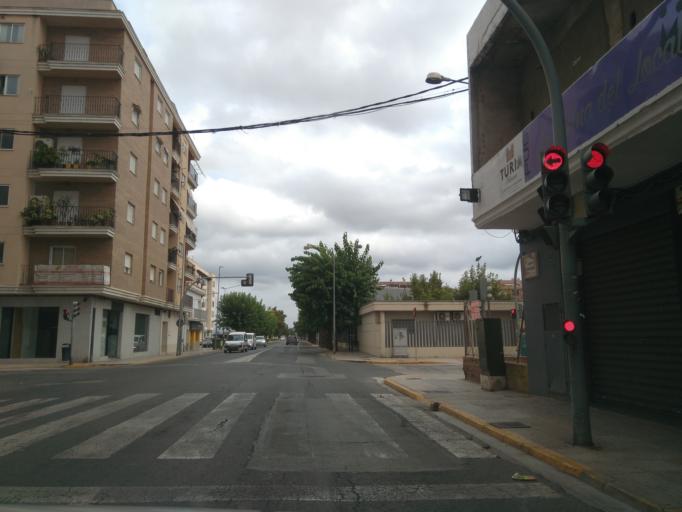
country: ES
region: Valencia
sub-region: Provincia de Valencia
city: Carlet
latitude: 39.2217
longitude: -0.5189
